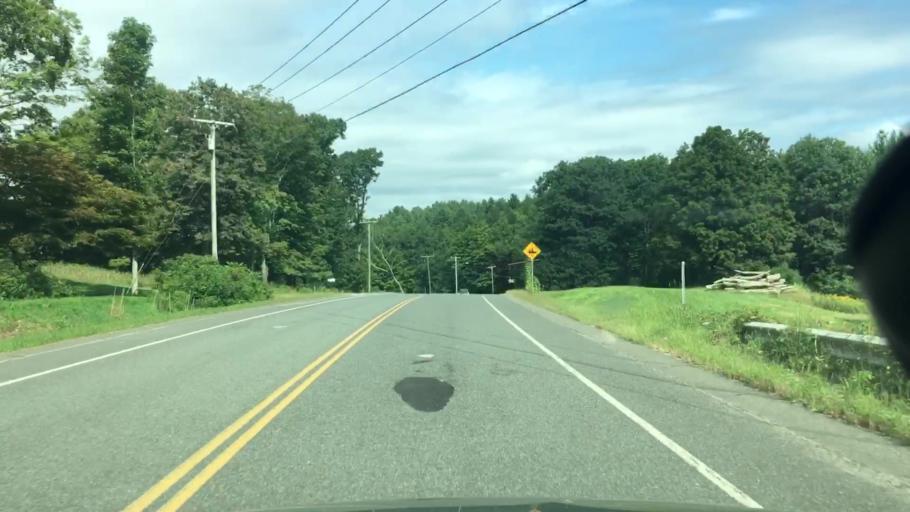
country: US
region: Massachusetts
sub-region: Franklin County
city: Colrain
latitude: 42.6654
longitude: -72.6822
